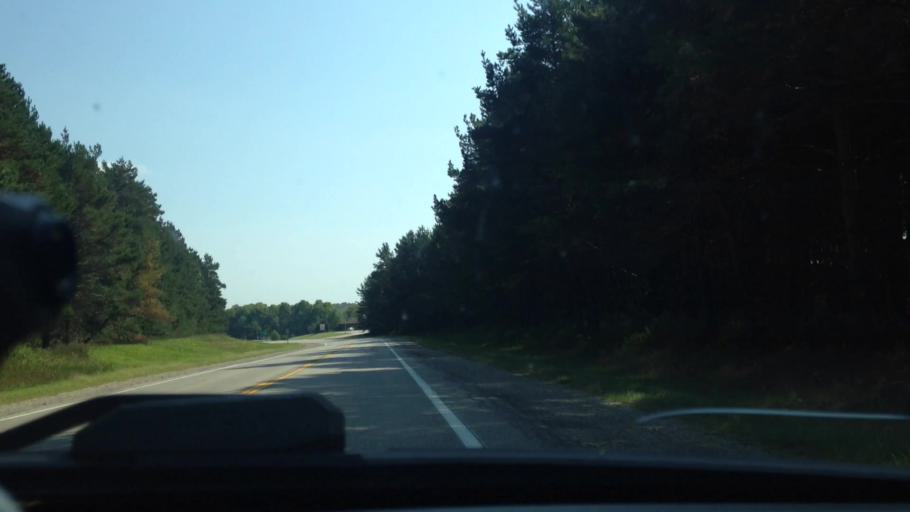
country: US
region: Michigan
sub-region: Luce County
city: Newberry
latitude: 46.3142
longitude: -85.6624
